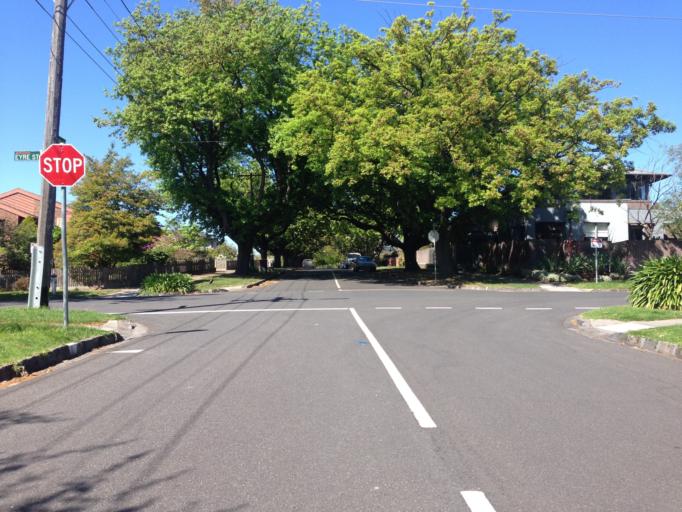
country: AU
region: Victoria
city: Balwyn
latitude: -37.8051
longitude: 145.0645
